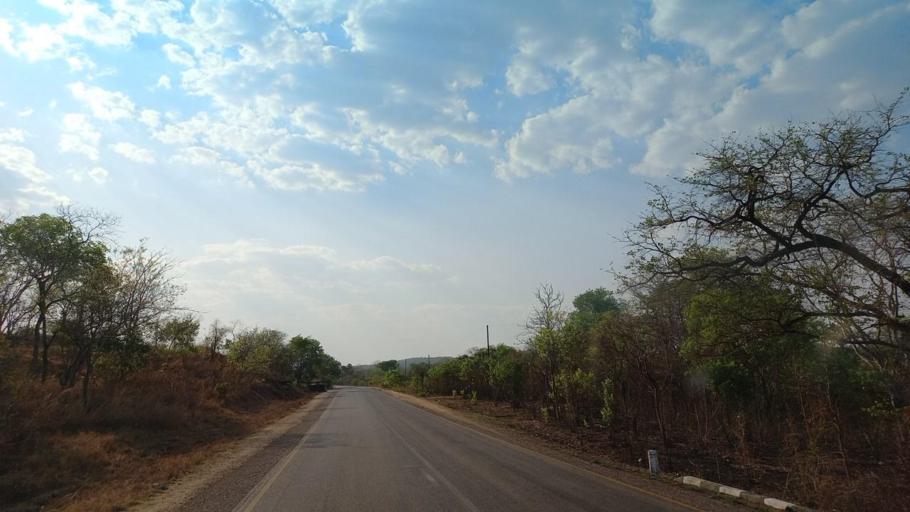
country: ZM
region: Lusaka
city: Luangwa
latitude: -14.9687
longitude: 30.0225
